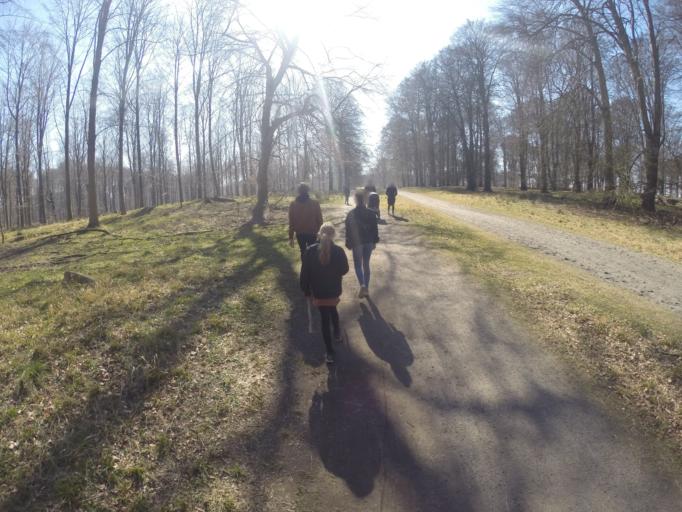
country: DK
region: Capital Region
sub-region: Lyngby-Tarbaek Kommune
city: Kongens Lyngby
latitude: 55.7788
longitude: 12.5495
